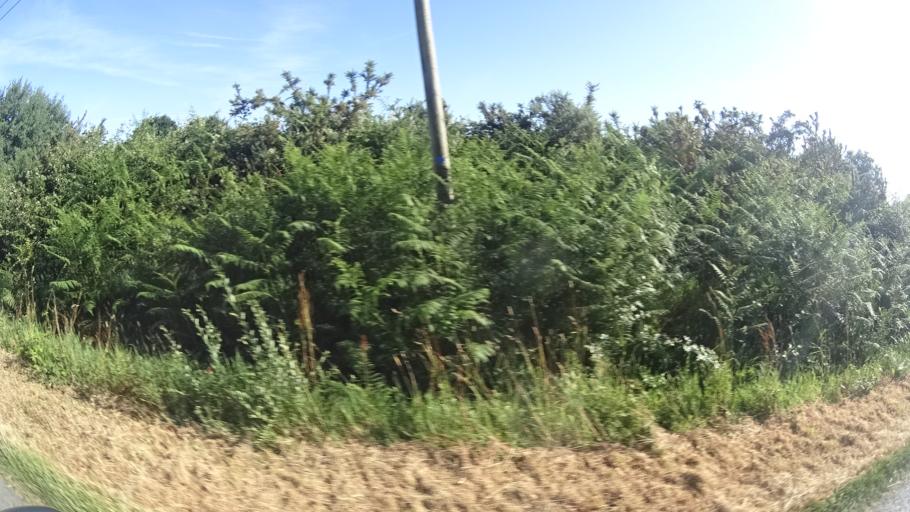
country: FR
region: Brittany
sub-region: Departement d'Ille-et-Vilaine
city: Grand-Fougeray
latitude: 47.7331
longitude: -1.7712
